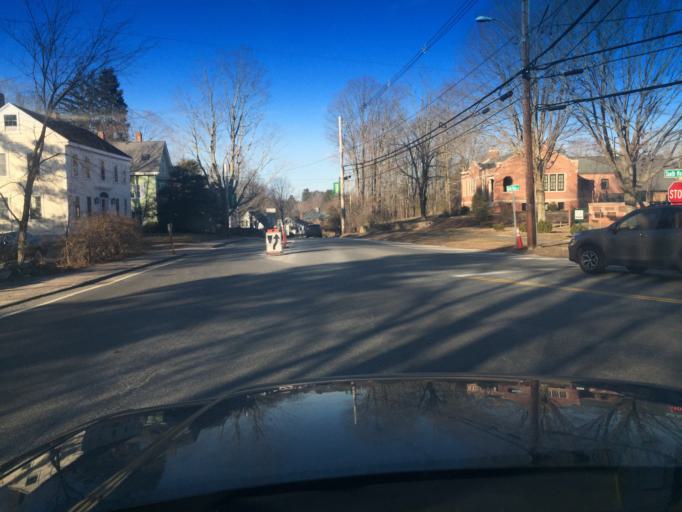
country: US
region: Massachusetts
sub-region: Middlesex County
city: Sherborn
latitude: 42.2423
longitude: -71.3704
